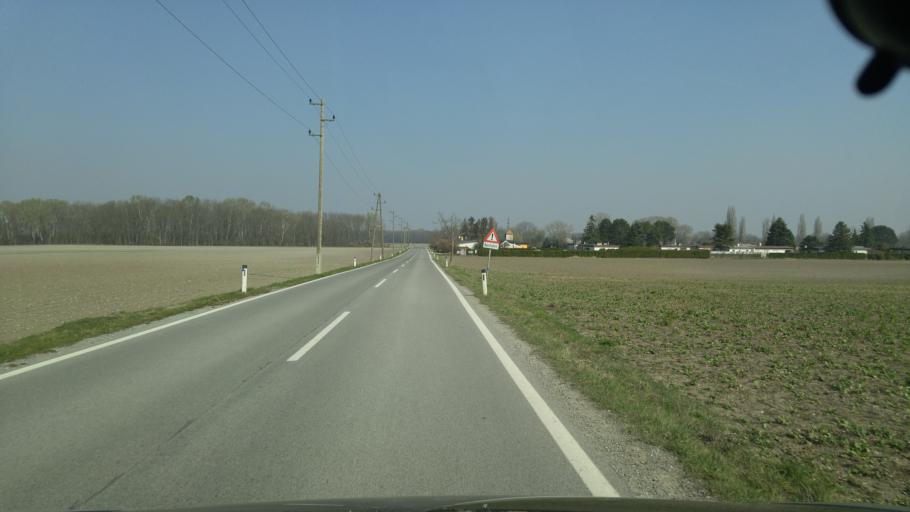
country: AT
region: Lower Austria
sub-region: Politischer Bezirk Wien-Umgebung
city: Moosbrunn
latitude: 48.0339
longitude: 16.4195
